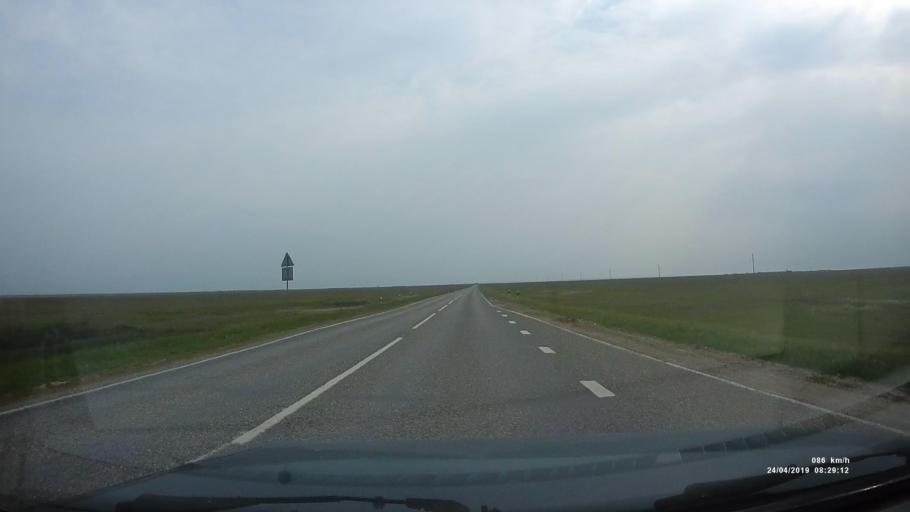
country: RU
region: Kalmykiya
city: Priyutnoye
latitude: 46.1504
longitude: 43.8272
